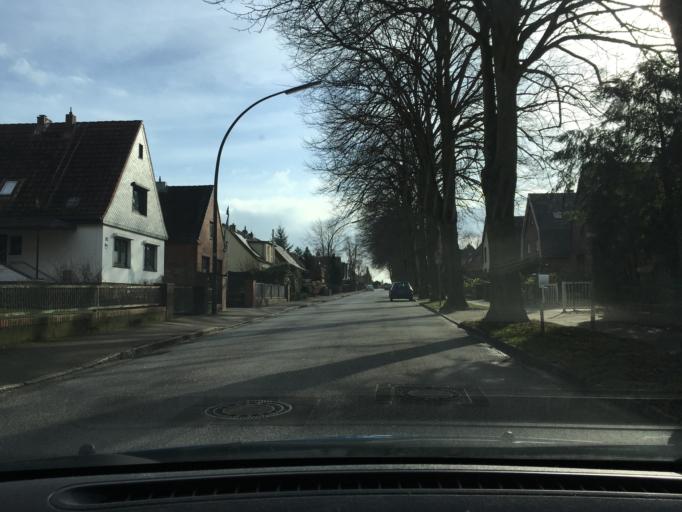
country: DE
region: Schleswig-Holstein
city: Wedel
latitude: 53.5831
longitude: 9.7217
